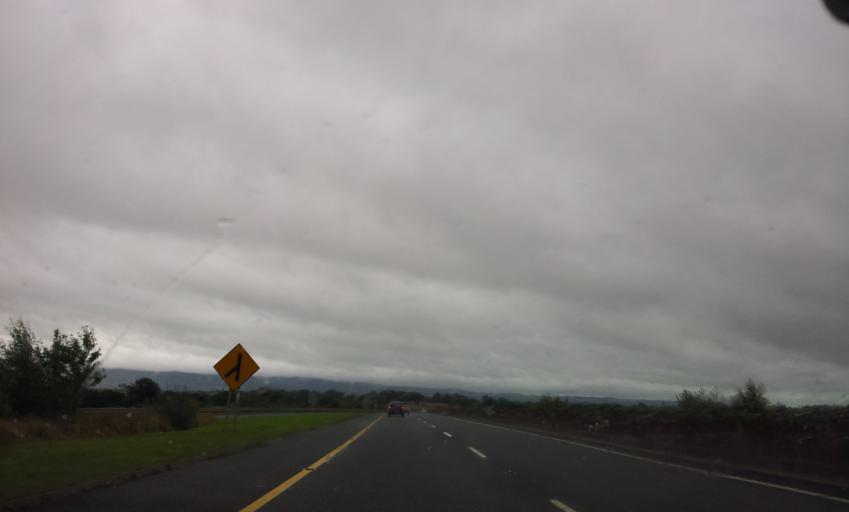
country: IE
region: Munster
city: Cahir
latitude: 52.3539
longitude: -8.0020
